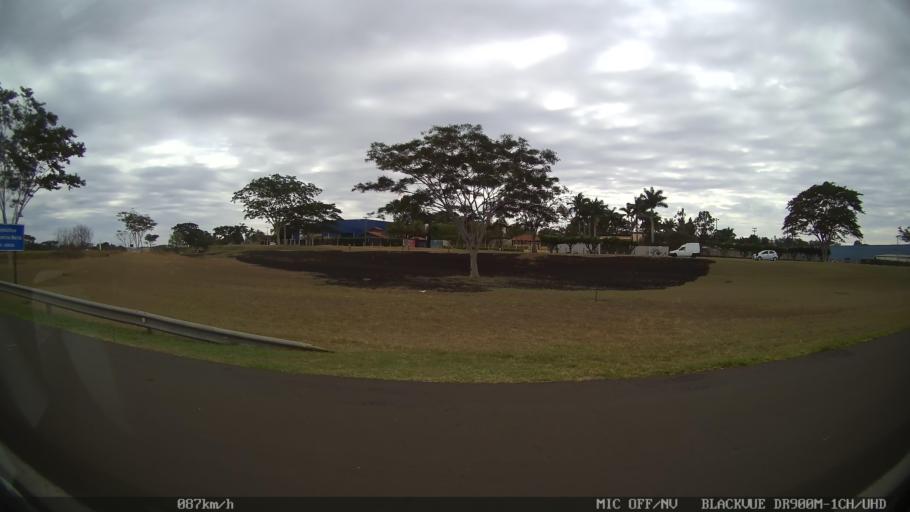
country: BR
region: Sao Paulo
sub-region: Bady Bassitt
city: Bady Bassitt
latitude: -20.8046
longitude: -49.5236
